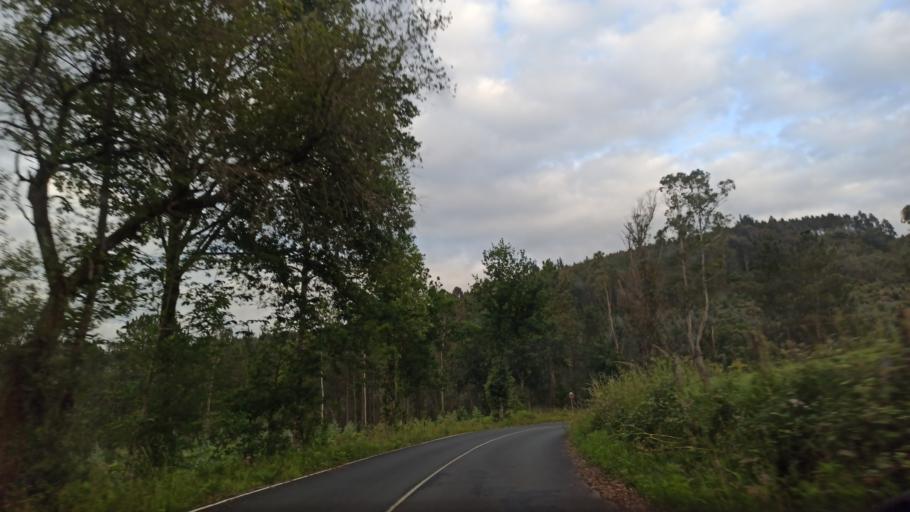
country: ES
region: Galicia
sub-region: Provincia da Coruna
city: Santiso
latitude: 42.8171
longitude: -8.1396
